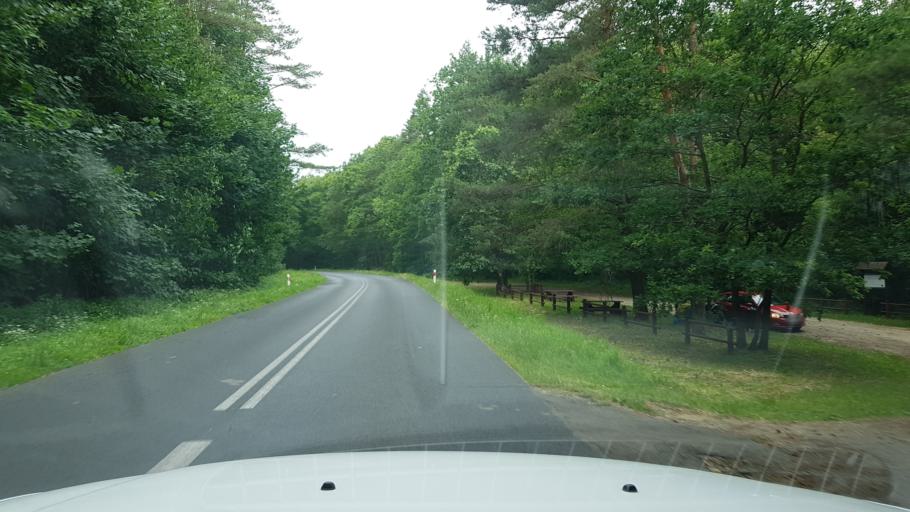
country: PL
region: West Pomeranian Voivodeship
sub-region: Powiat gryficki
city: Cerkwica
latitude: 53.9289
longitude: 15.0881
